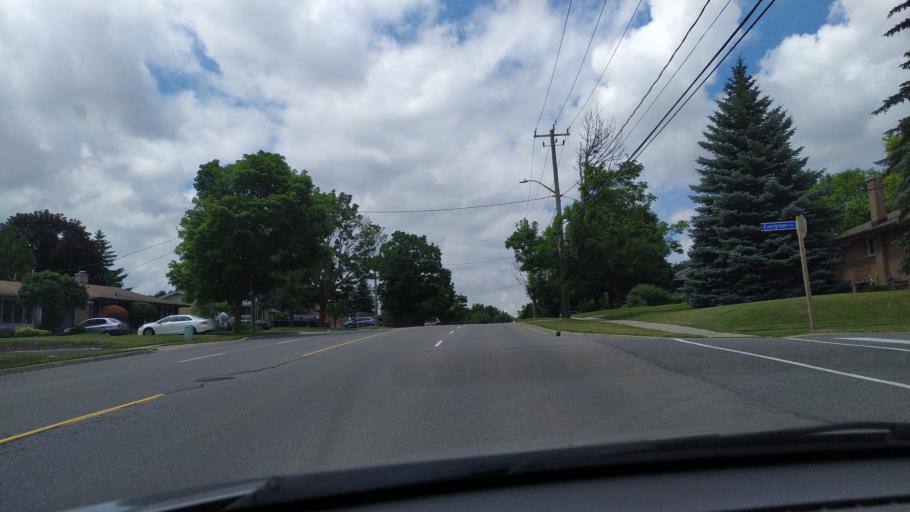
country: CA
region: Ontario
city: Kitchener
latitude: 43.4288
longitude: -80.5073
